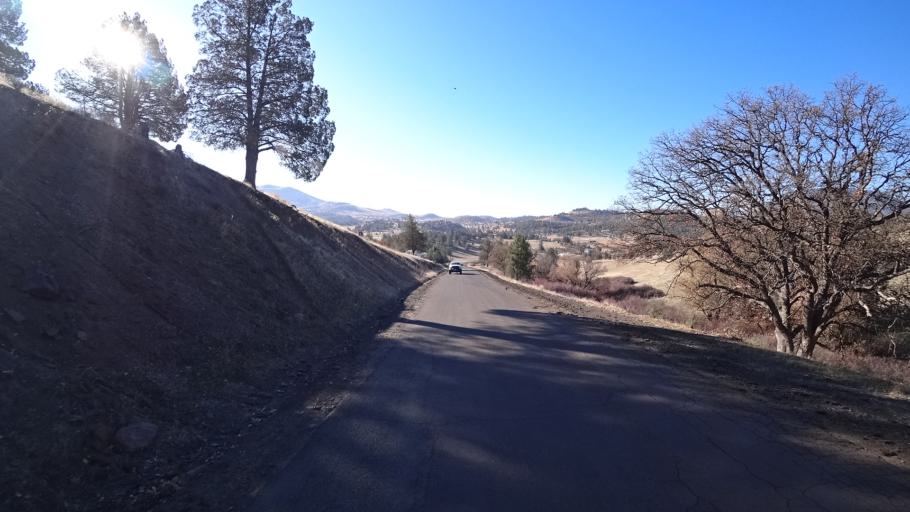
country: US
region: California
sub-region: Siskiyou County
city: Montague
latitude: 41.8980
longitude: -122.4240
